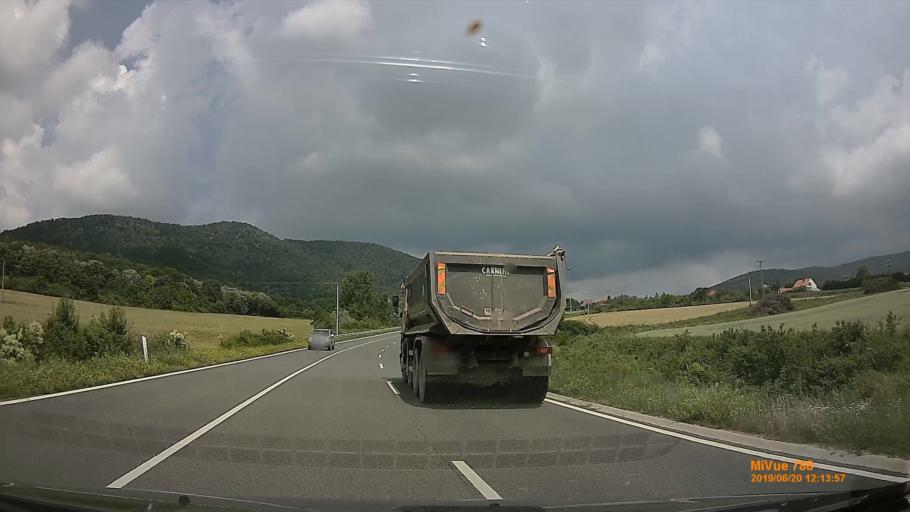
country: HU
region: Baranya
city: Hosszuheteny
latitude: 46.1633
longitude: 18.3423
